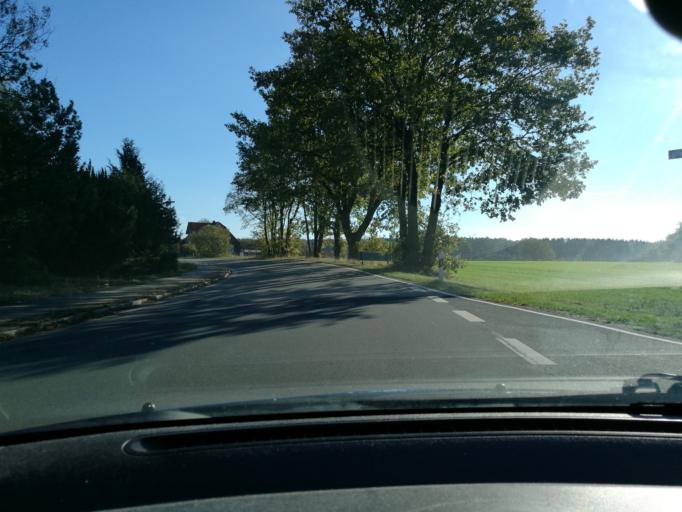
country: DE
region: Lower Saxony
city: Nahrendorf
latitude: 53.1578
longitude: 10.8121
